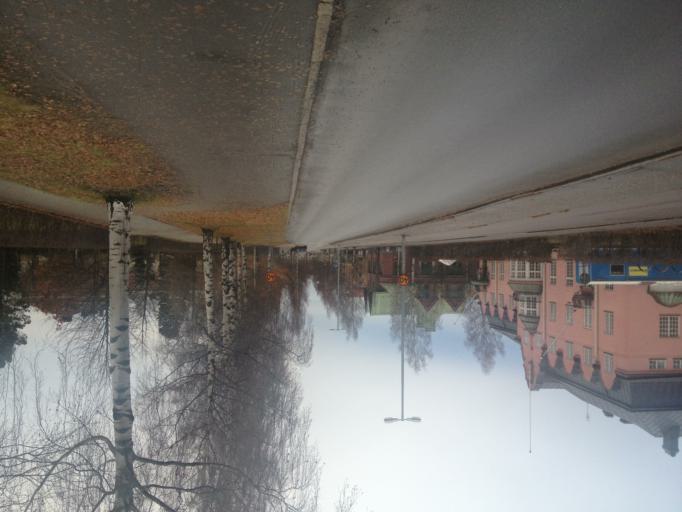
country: SE
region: Vaesterbotten
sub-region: Umea Kommun
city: Umea
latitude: 63.8237
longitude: 20.2701
